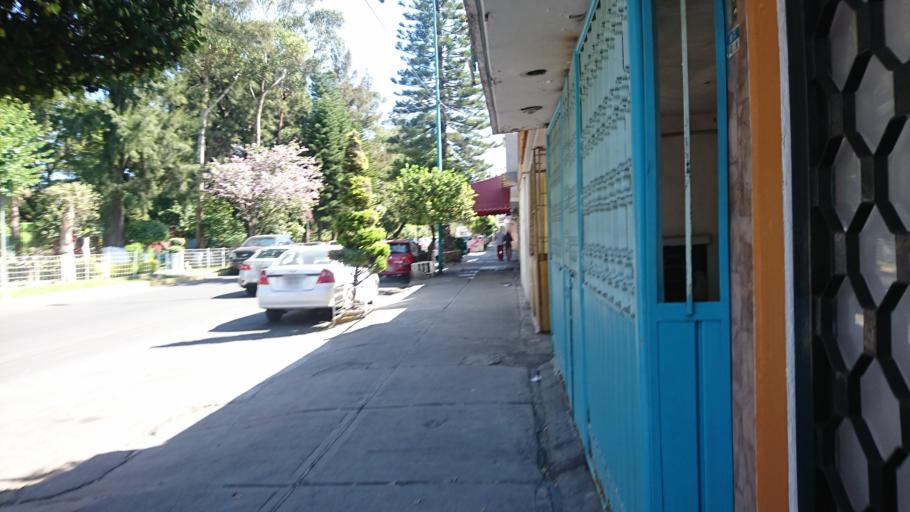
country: MX
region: Mexico City
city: Iztapalapa
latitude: 19.3247
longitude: -99.1063
